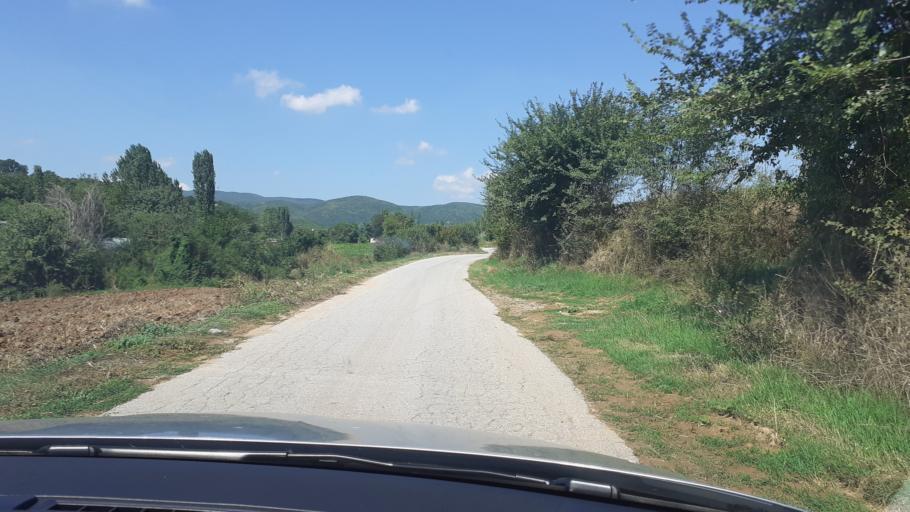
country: MK
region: Strumica
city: Veljusa
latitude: 41.5199
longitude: 22.5979
